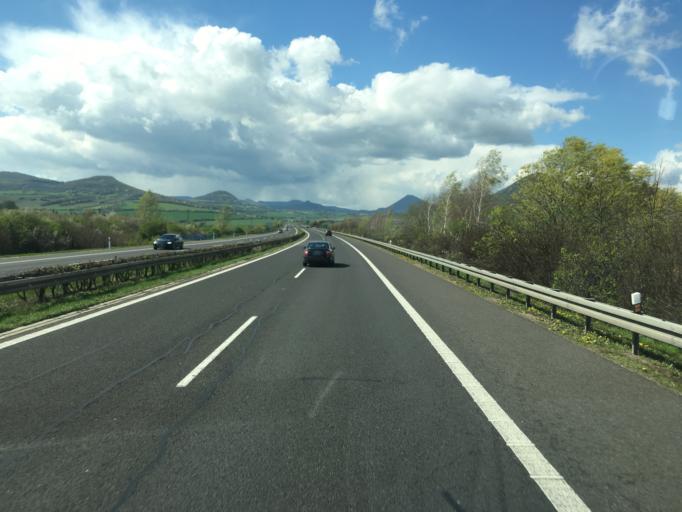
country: CZ
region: Ustecky
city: Lovosice
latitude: 50.5022
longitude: 14.0585
